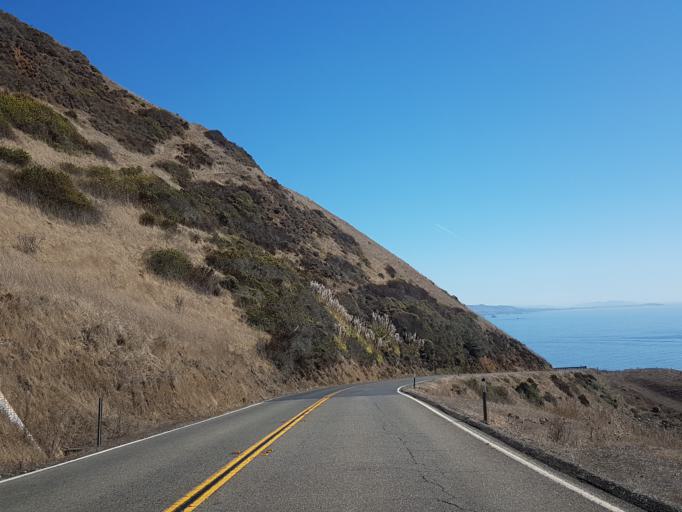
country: US
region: California
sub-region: Sonoma County
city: Monte Rio
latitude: 38.4941
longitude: -123.1978
